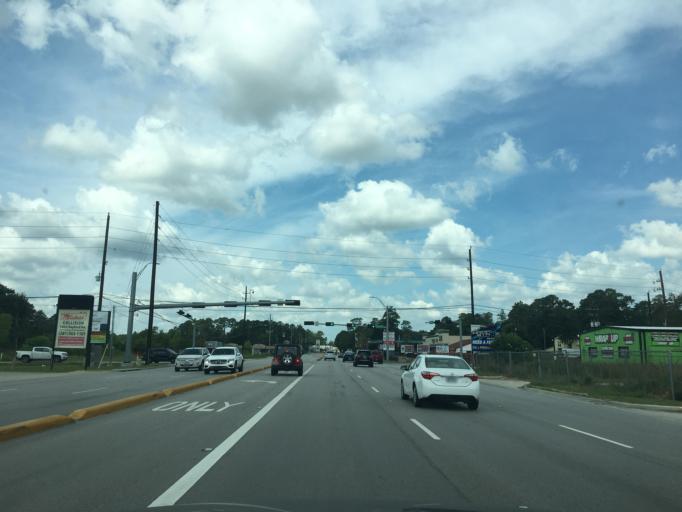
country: US
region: Texas
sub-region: Montgomery County
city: Oak Ridge North
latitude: 30.1251
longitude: -95.4175
